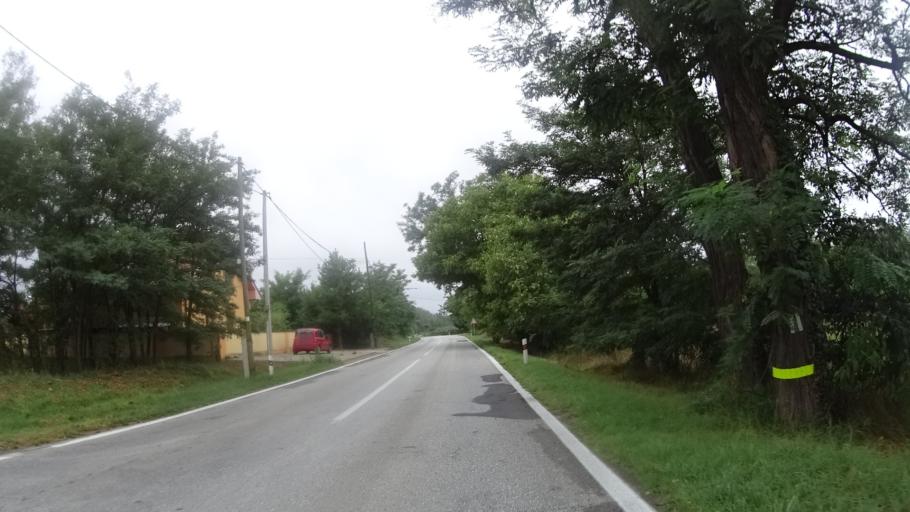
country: HU
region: Komarom-Esztergom
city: Neszmely
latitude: 47.7540
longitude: 18.3907
